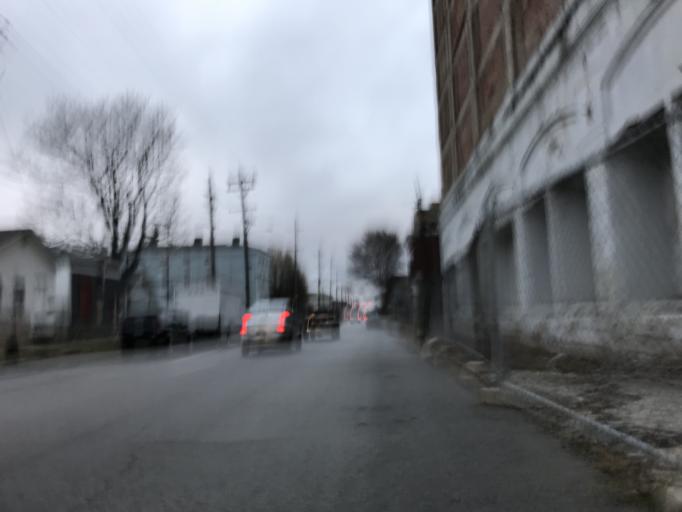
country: US
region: Kentucky
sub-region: Jefferson County
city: Louisville
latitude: 38.2407
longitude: -85.7388
